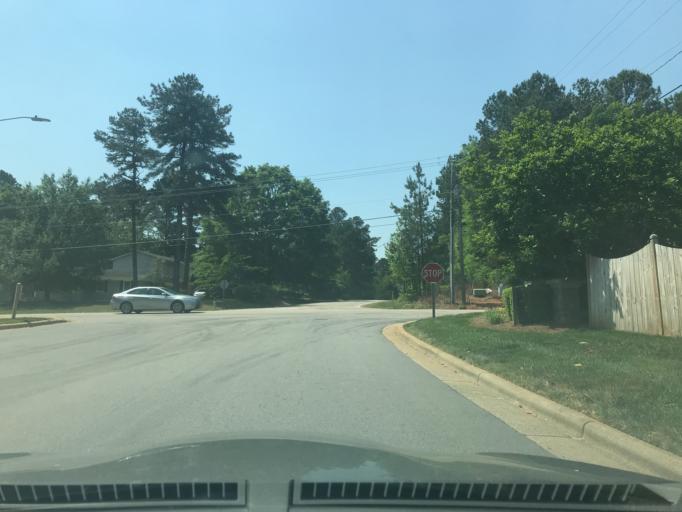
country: US
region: North Carolina
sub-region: Wake County
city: West Raleigh
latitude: 35.8854
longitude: -78.5953
